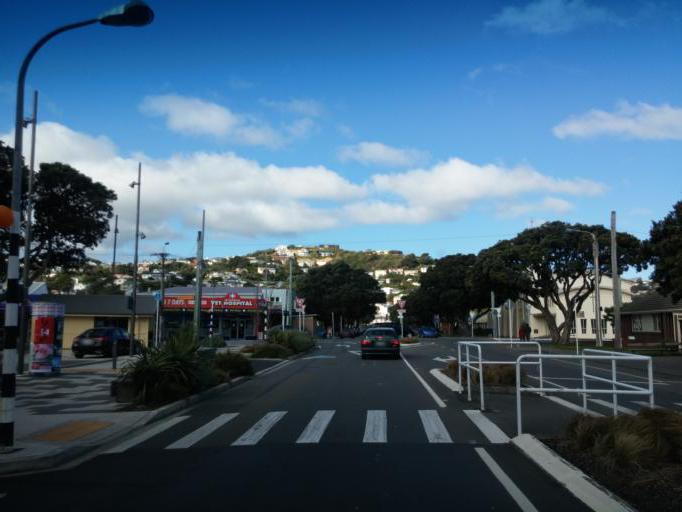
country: NZ
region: Wellington
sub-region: Wellington City
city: Wellington
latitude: -41.3161
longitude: 174.8160
